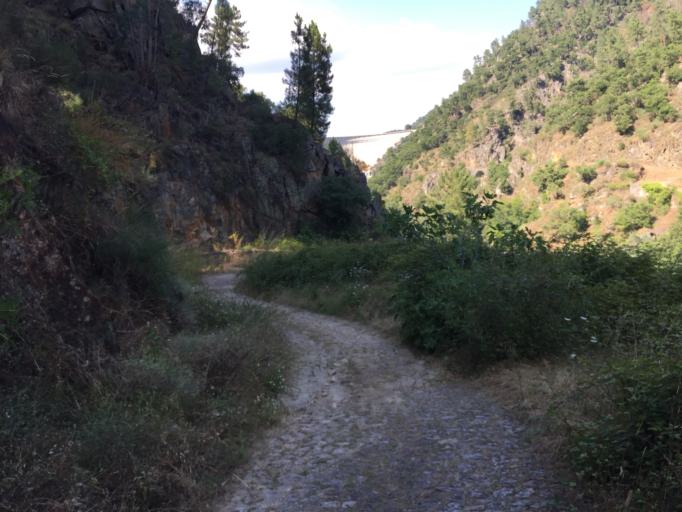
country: PT
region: Leiria
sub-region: Pedrogao Grande
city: Pedrogao Grande
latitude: 39.9050
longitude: -8.1404
